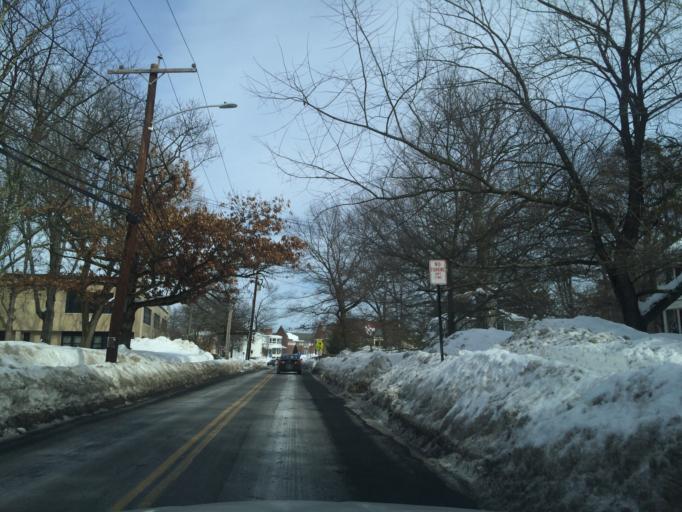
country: US
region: Massachusetts
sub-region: Middlesex County
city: Waltham
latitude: 42.3415
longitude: -71.2503
